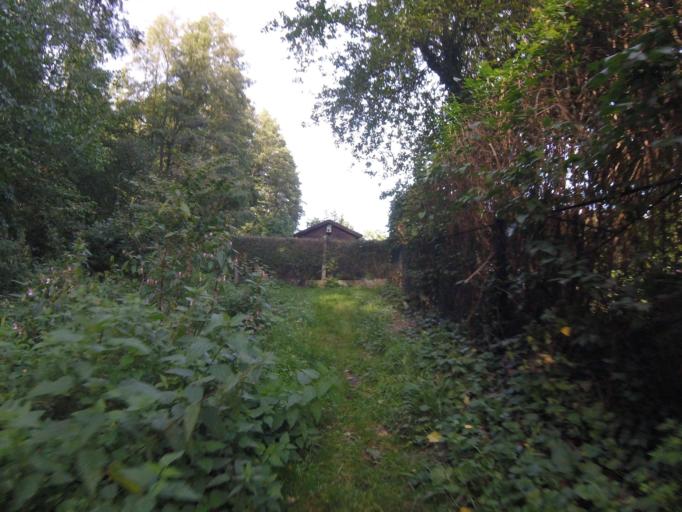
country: DE
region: Brandenburg
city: Bestensee
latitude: 52.2788
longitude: 13.6510
